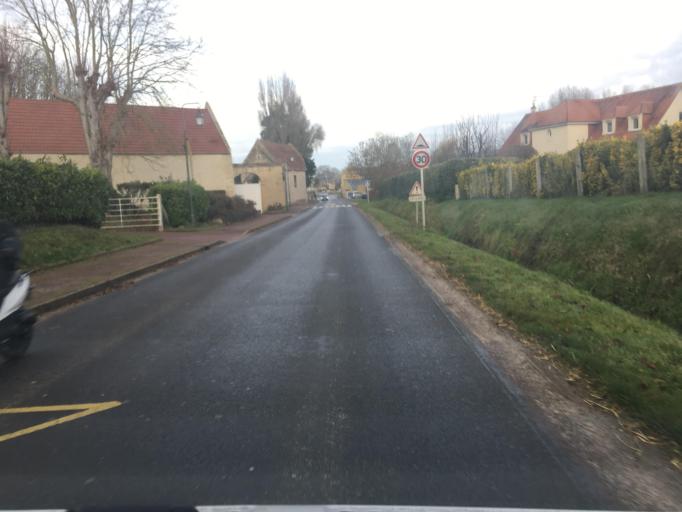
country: FR
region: Lower Normandy
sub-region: Departement du Calvados
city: Ver-sur-Mer
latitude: 49.3132
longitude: -0.5488
